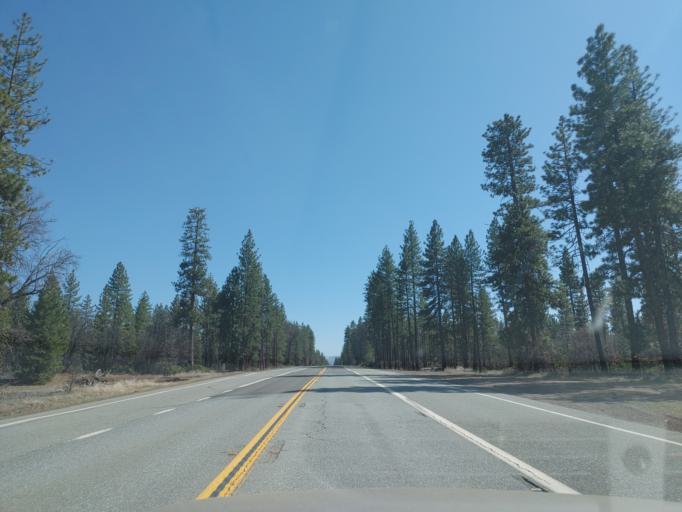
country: US
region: California
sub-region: Shasta County
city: Burney
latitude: 40.9703
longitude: -121.6192
